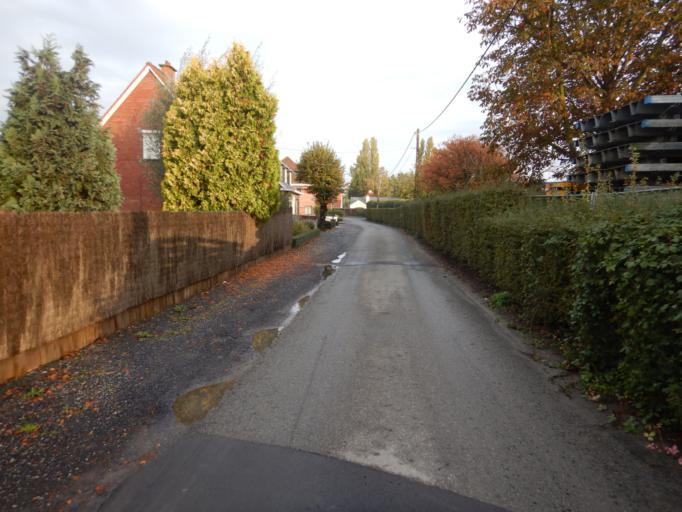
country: BE
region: Flanders
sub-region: Provincie West-Vlaanderen
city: Roeselare
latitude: 50.9409
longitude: 3.1554
